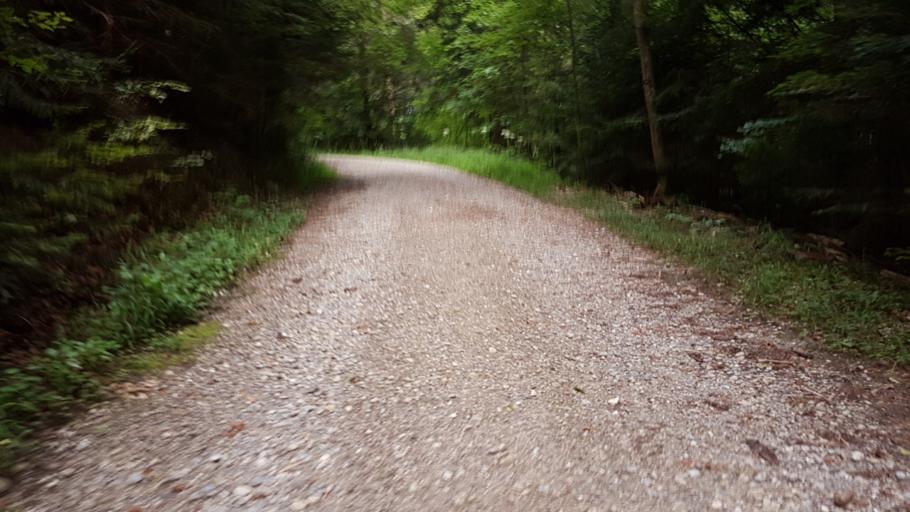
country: CH
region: Lucerne
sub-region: Entlebuch District
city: Oberdiessbach
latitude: 46.8587
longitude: 7.6367
